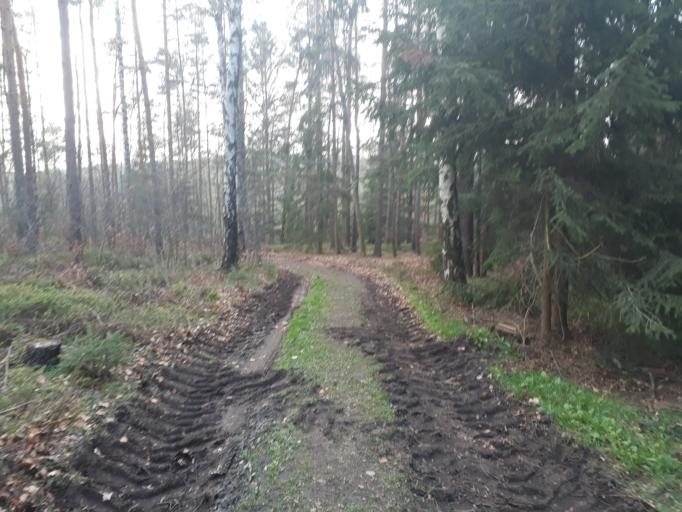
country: DE
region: Saxony
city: Reinhardtsgrimma
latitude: 50.8925
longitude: 13.7821
